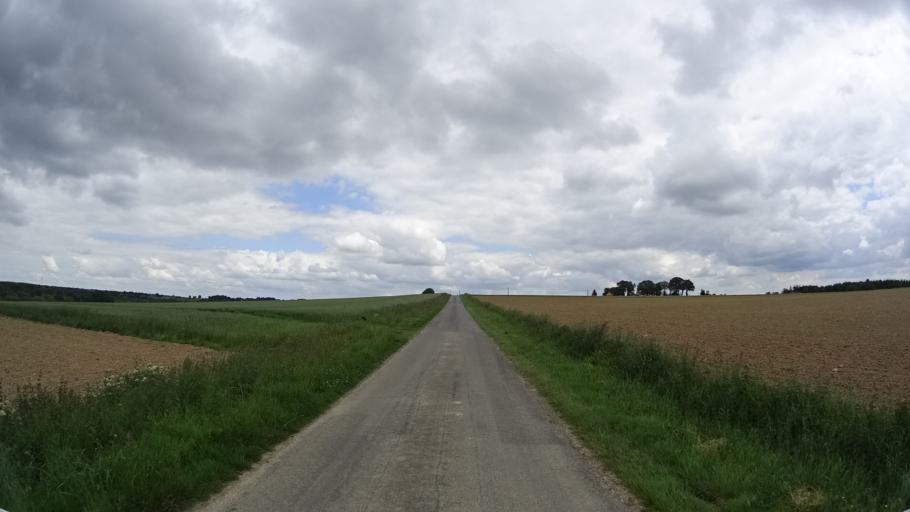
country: FR
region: Brittany
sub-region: Departement d'Ille-et-Vilaine
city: Monterfil
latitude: 48.0667
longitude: -2.0253
